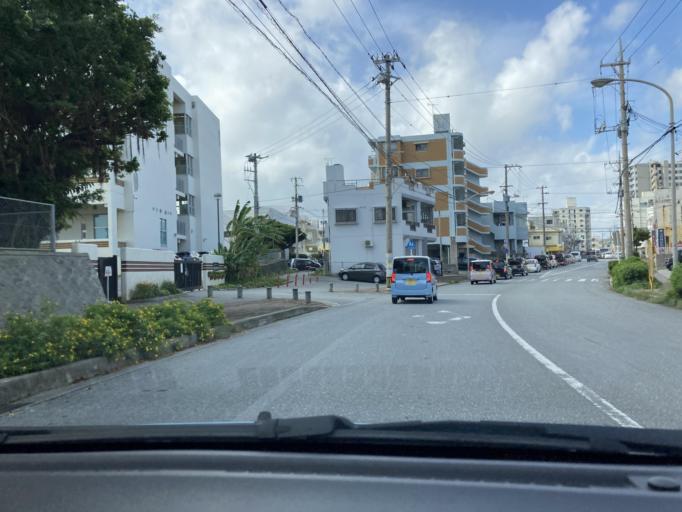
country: JP
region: Okinawa
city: Ginowan
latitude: 26.2612
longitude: 127.7454
